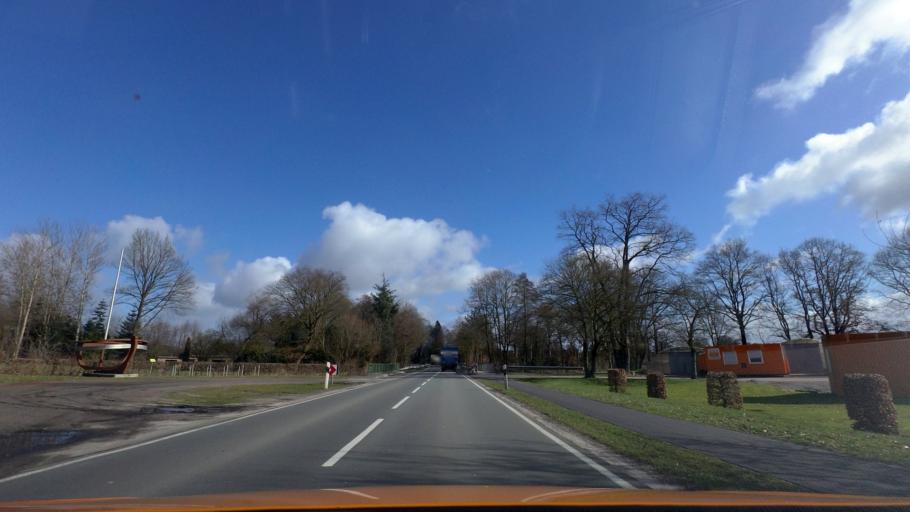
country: DE
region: Lower Saxony
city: Edewecht
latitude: 53.1131
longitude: 7.9606
